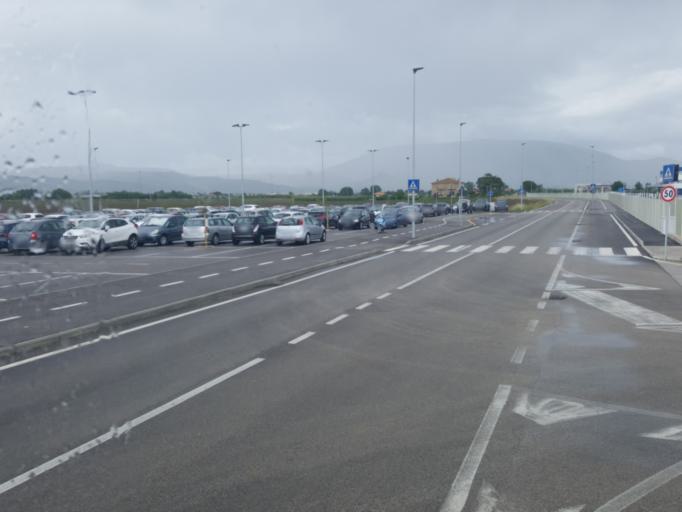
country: IT
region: Umbria
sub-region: Provincia di Perugia
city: Ospedalicchio
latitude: 43.0715
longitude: 12.5018
